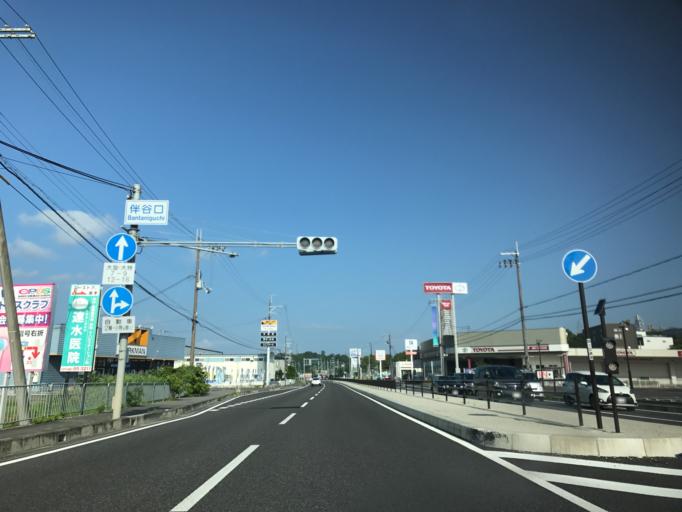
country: JP
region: Shiga Prefecture
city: Minakuchicho-matoba
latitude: 34.9845
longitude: 136.1355
